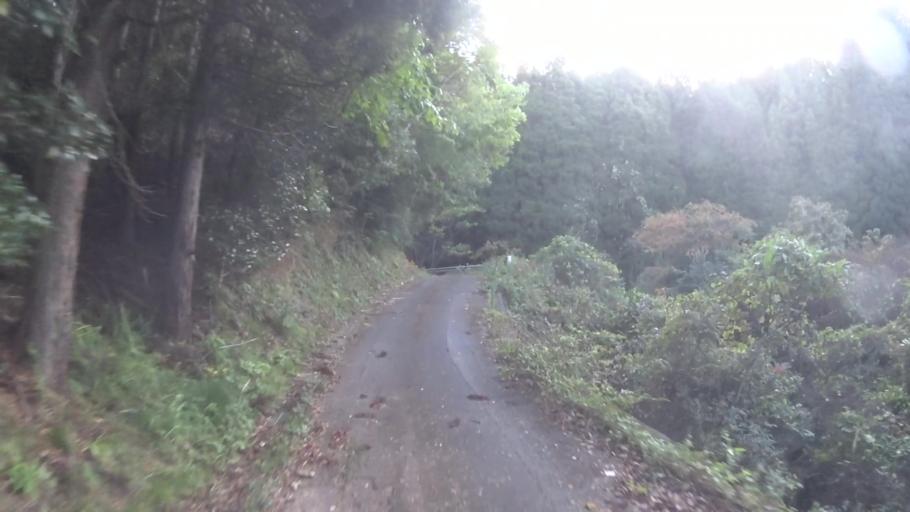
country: JP
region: Kyoto
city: Ayabe
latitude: 35.2720
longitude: 135.2491
